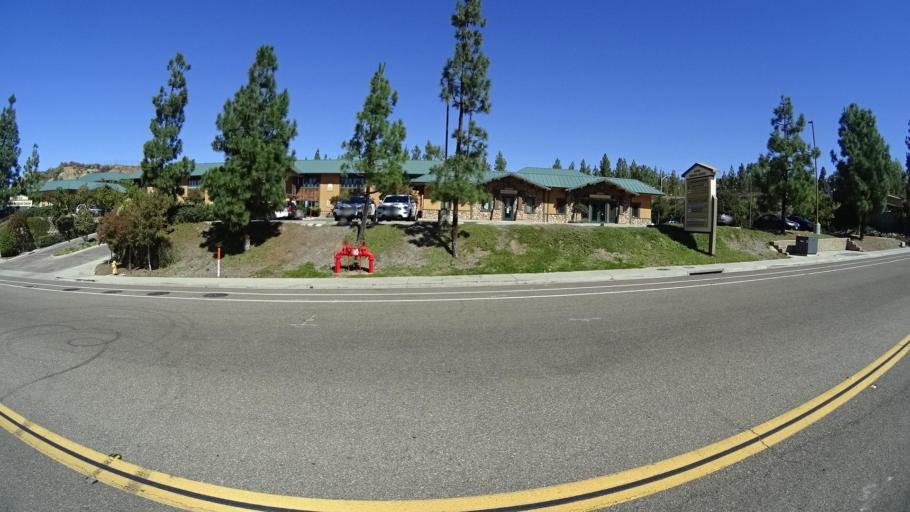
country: US
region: California
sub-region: San Diego County
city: Alpine
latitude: 32.8377
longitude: -116.7797
